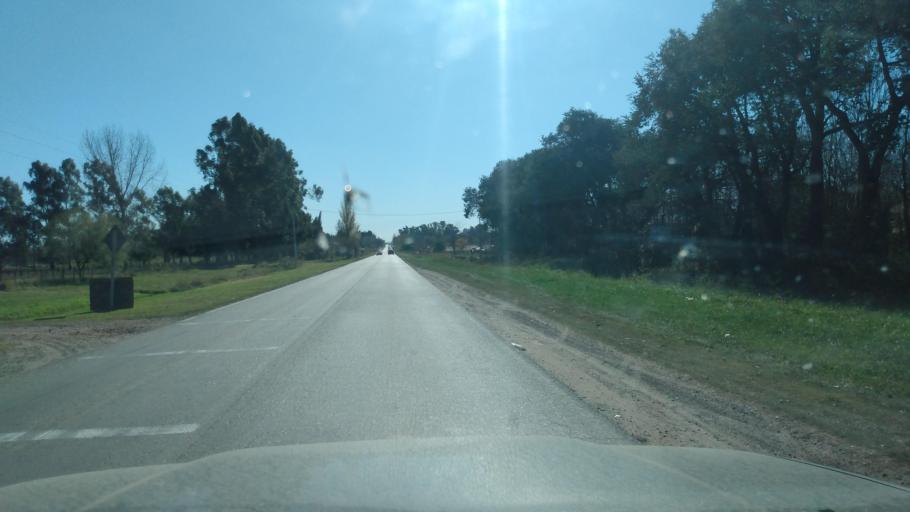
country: AR
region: Buenos Aires
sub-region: Partido de Lujan
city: Lujan
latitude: -34.5288
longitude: -59.1692
